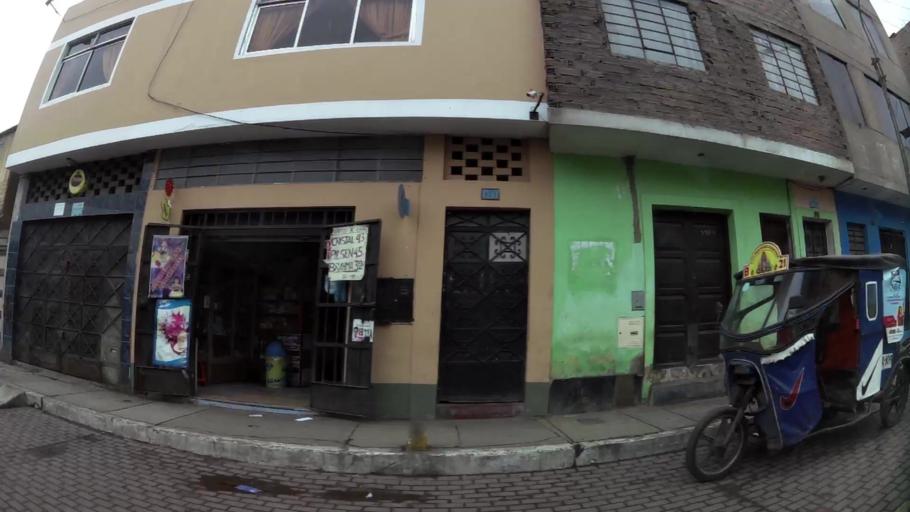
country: PE
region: Lima
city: Lima
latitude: -12.0522
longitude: -77.0065
